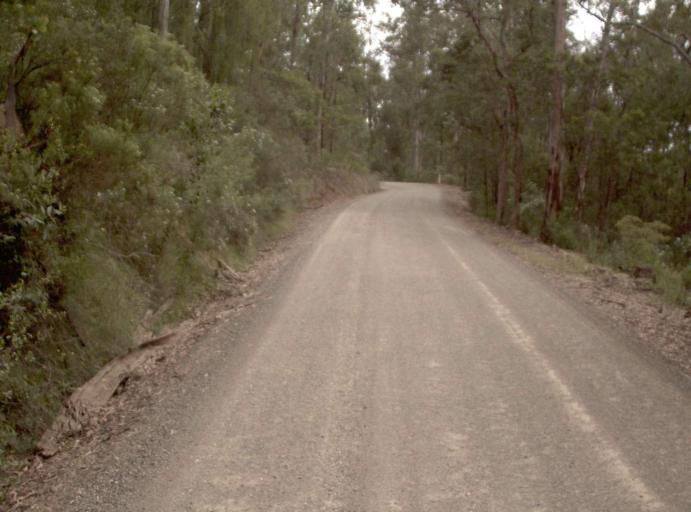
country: AU
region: Victoria
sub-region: East Gippsland
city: Bairnsdale
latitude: -37.7004
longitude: 147.5878
